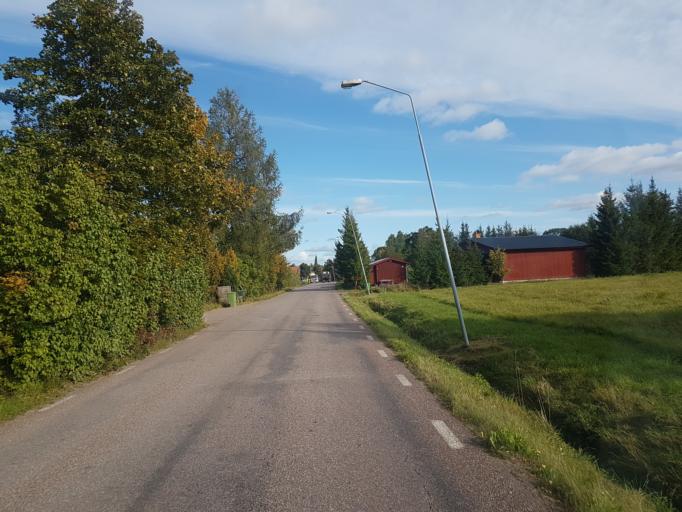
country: SE
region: Dalarna
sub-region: Saters Kommun
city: Saeter
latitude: 60.4021
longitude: 15.6308
